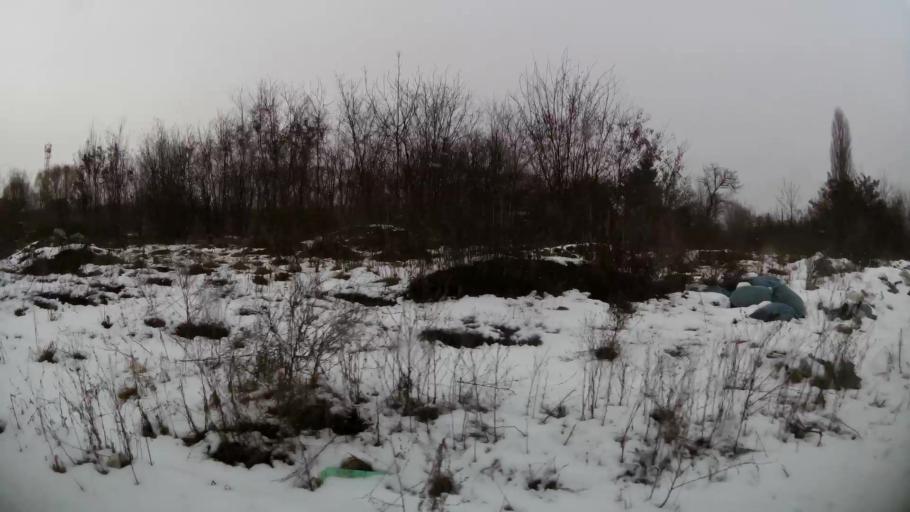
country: RO
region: Ilfov
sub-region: Comuna Mogosoaia
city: Mogosoaia
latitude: 44.5131
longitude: 26.0275
